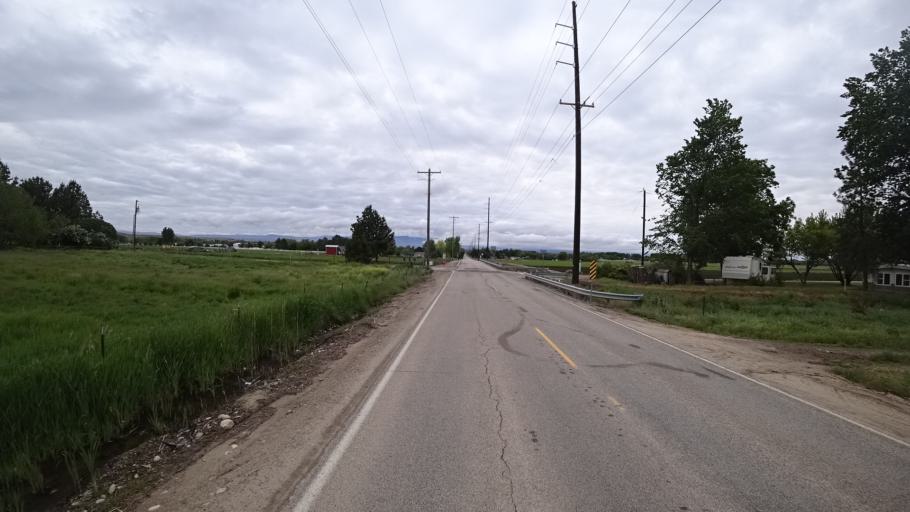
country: US
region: Idaho
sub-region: Ada County
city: Eagle
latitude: 43.7210
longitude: -116.4240
